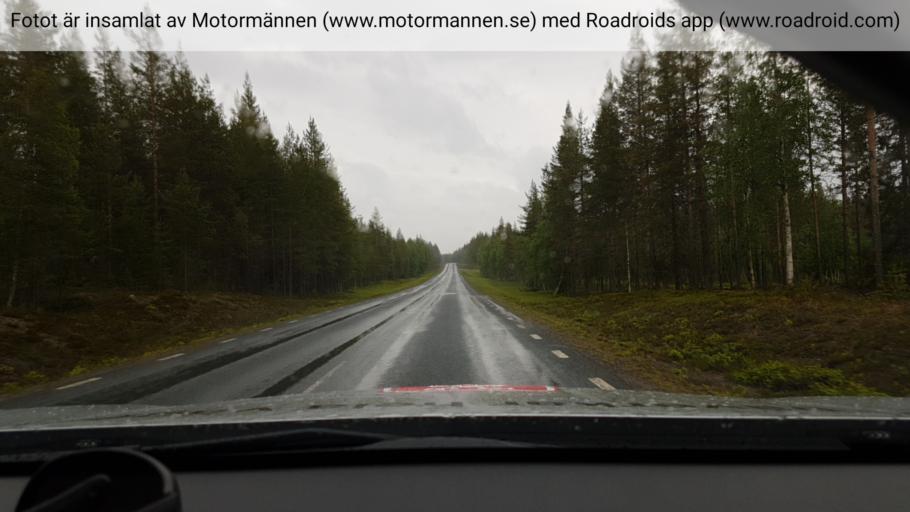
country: SE
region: Vaesterbotten
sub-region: Mala Kommun
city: Mala
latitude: 65.2198
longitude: 18.6525
